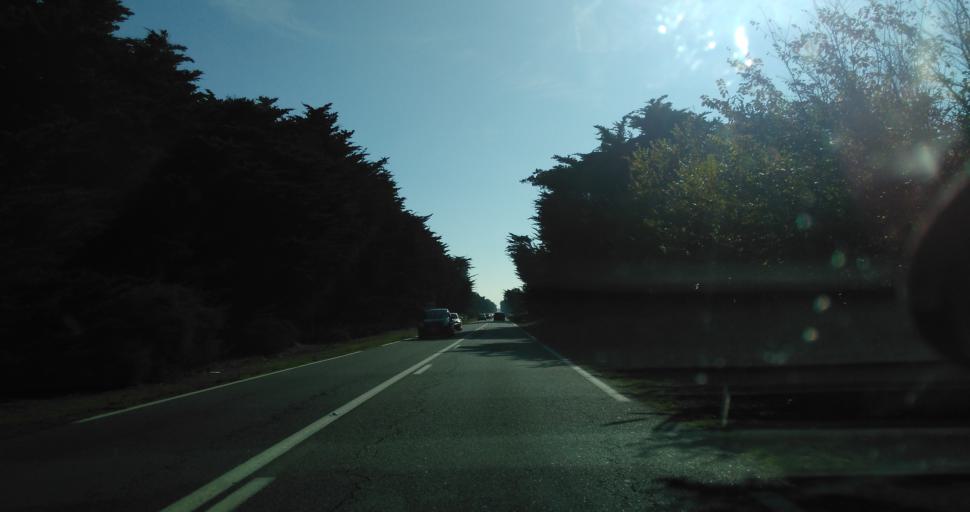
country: FR
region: Brittany
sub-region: Departement du Morbihan
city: Plouharnel
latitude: 47.5740
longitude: -3.1347
